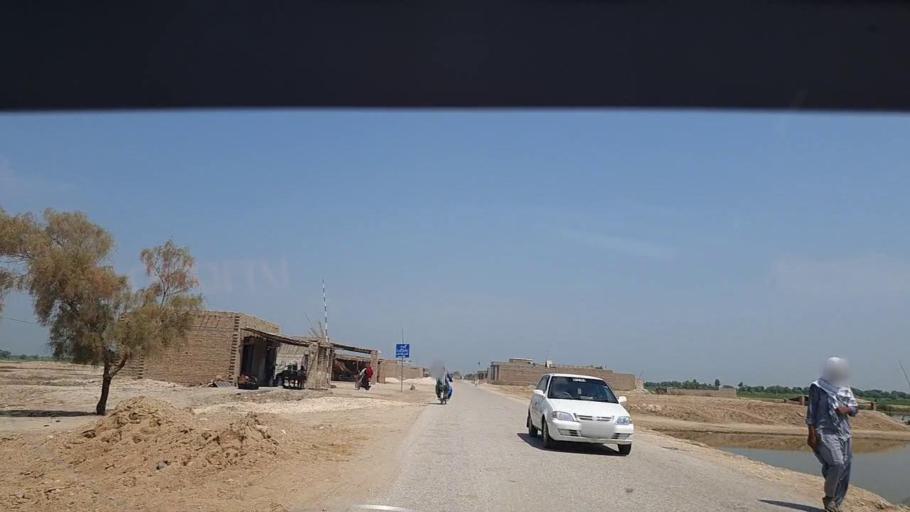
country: PK
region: Sindh
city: Thul
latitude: 28.1225
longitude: 68.8157
